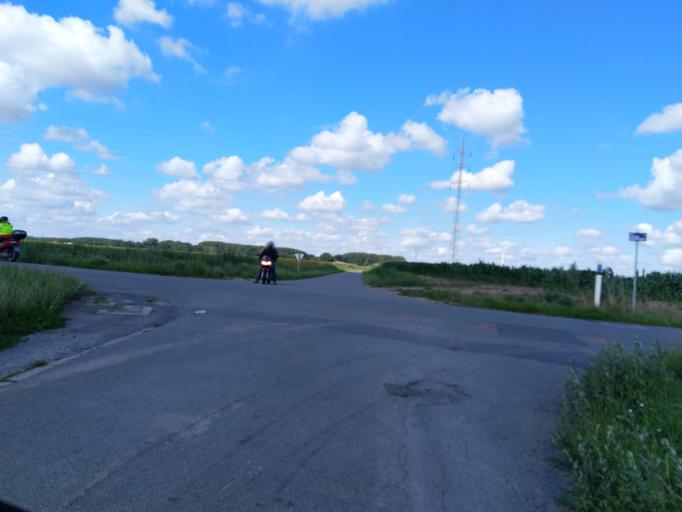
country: BE
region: Wallonia
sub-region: Province du Hainaut
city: Beloeil
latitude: 50.6021
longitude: 3.6945
